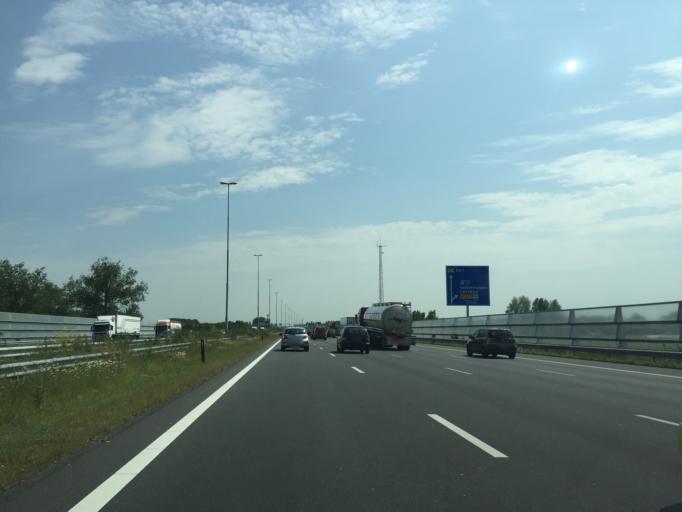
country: NL
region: Gelderland
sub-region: Gemeente Culemborg
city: Culemborg
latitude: 51.8858
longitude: 5.2027
